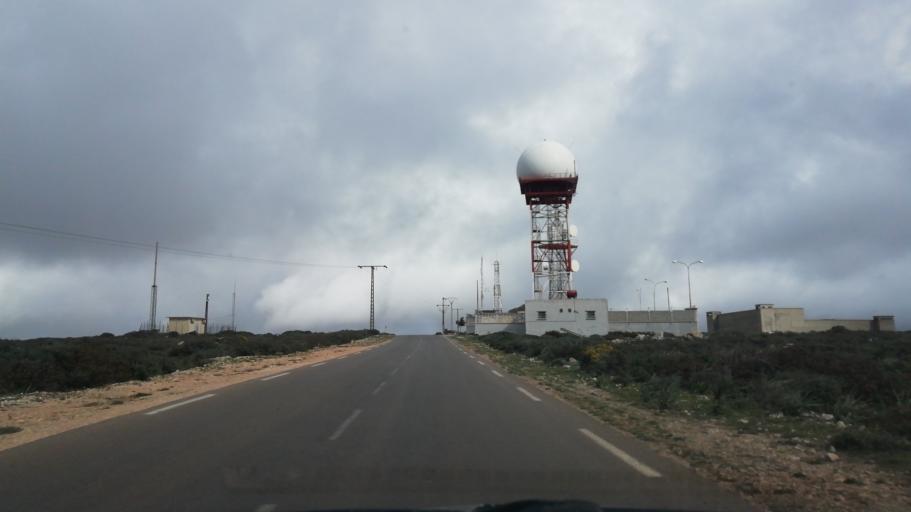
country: DZ
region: Oran
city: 'Ain el Turk
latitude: 35.6955
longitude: -0.7722
